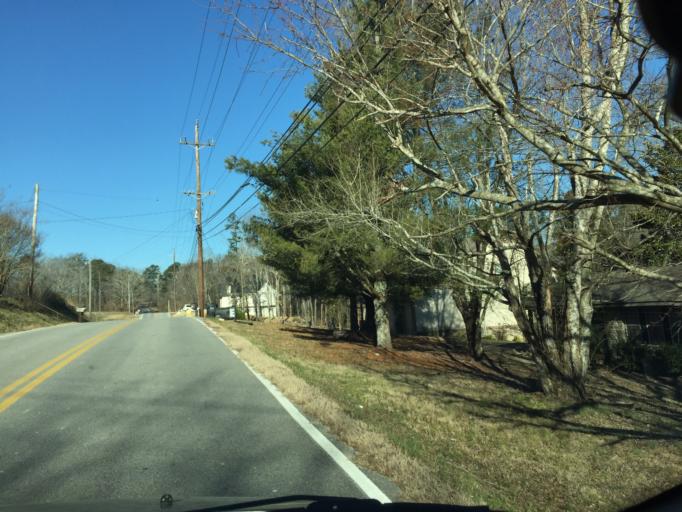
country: US
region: Tennessee
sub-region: Hamilton County
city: Collegedale
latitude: 35.0378
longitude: -85.0892
